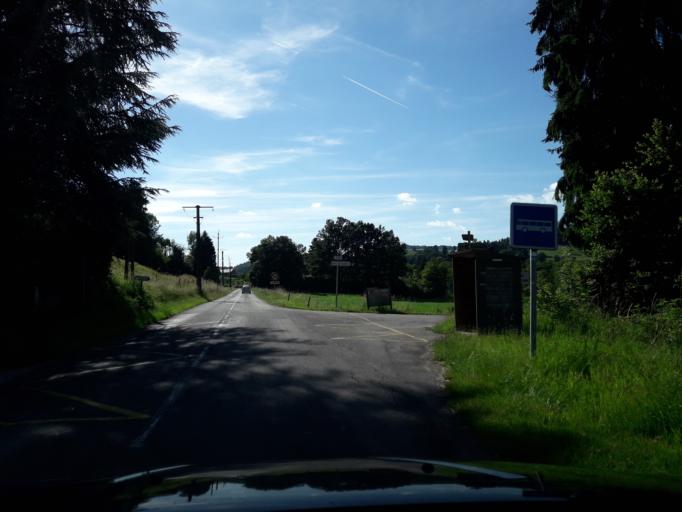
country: FR
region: Rhone-Alpes
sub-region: Departement de la Savoie
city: La Bridoire
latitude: 45.5397
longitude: 5.7777
